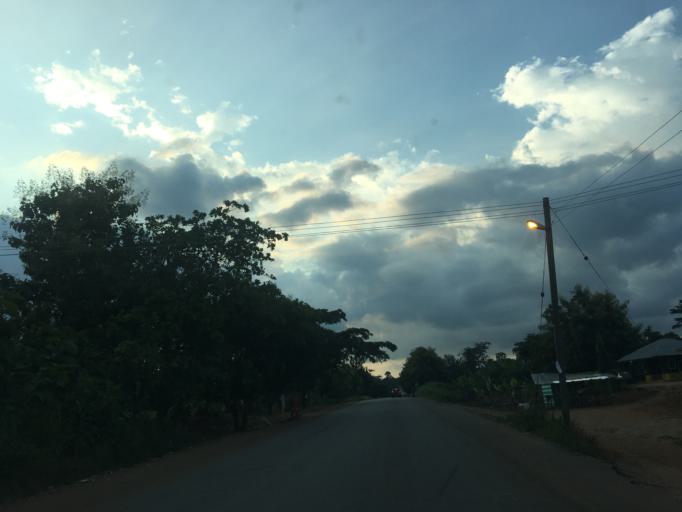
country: GH
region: Western
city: Bibiani
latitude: 6.7015
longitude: -2.4485
